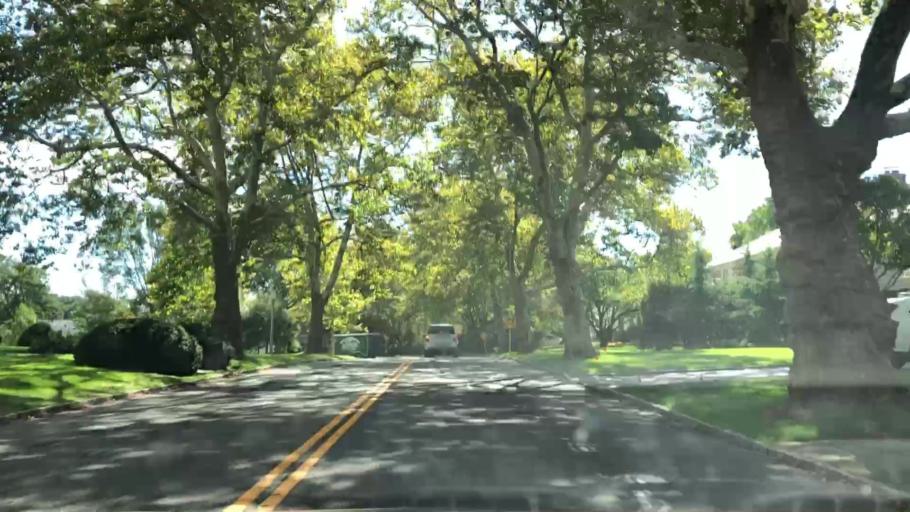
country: US
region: New York
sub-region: Nassau County
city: Munsey Park
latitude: 40.7987
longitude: -73.6723
